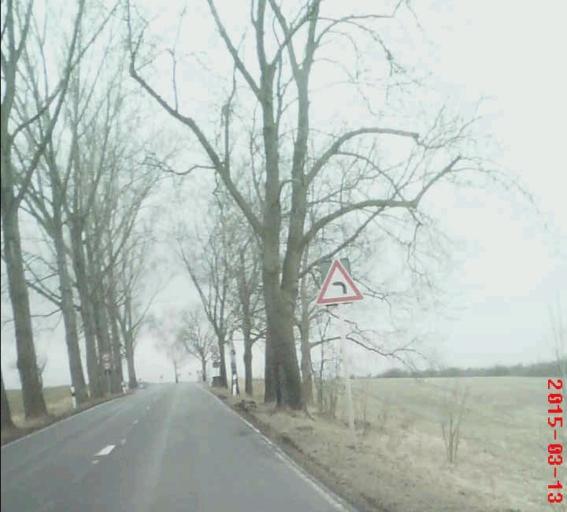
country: DE
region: Thuringia
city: Schonstedt
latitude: 51.0787
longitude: 10.6019
